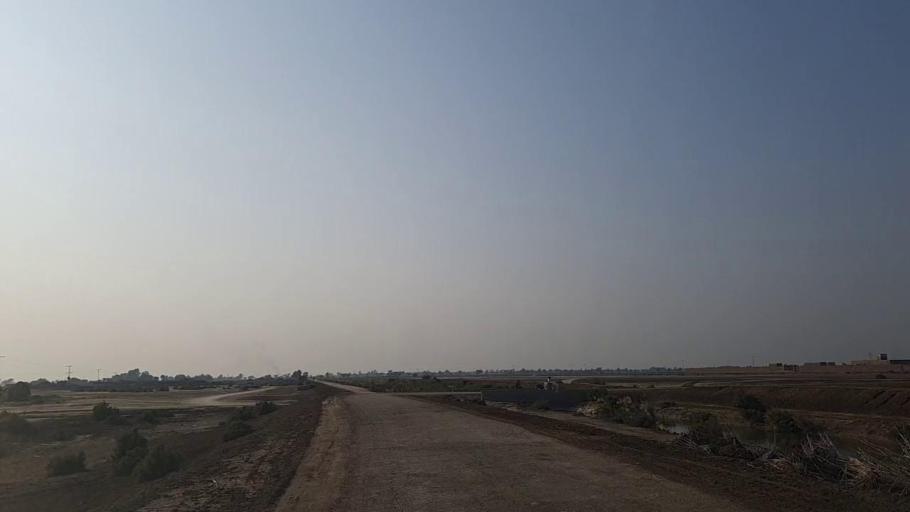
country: PK
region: Sindh
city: Jam Sahib
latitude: 26.2867
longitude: 68.6093
